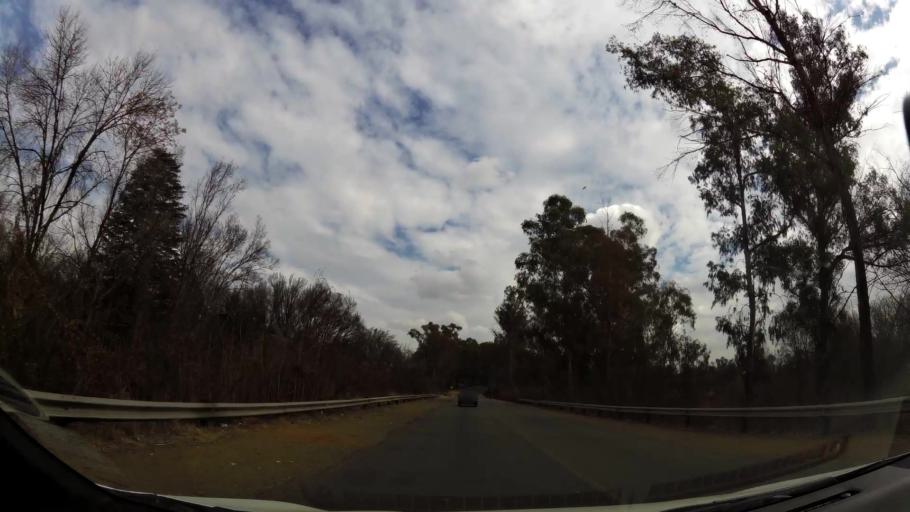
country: ZA
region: Gauteng
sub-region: Sedibeng District Municipality
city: Meyerton
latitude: -26.4177
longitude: 28.0925
